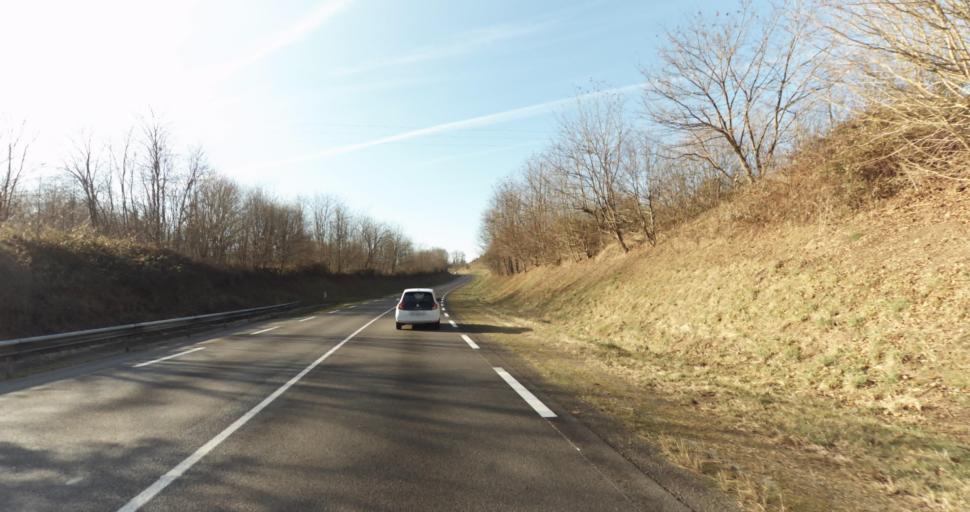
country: FR
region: Limousin
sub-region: Departement de la Haute-Vienne
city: Saint-Priest-sous-Aixe
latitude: 45.8055
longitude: 1.1149
